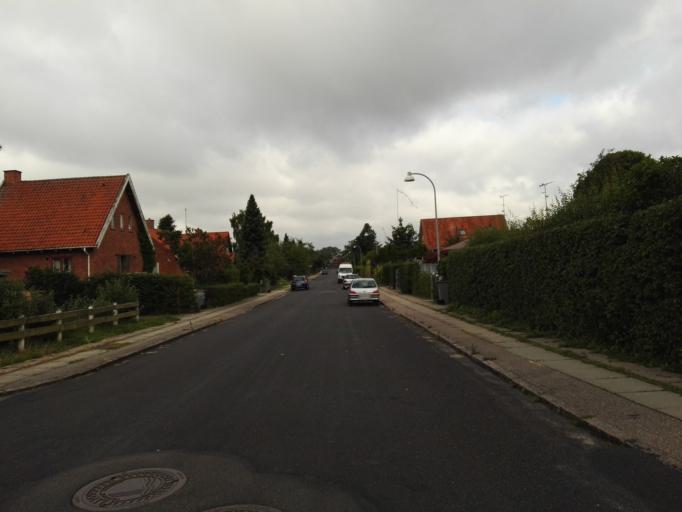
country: DK
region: Capital Region
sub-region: Ballerup Kommune
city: Ballerup
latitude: 55.7230
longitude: 12.3520
